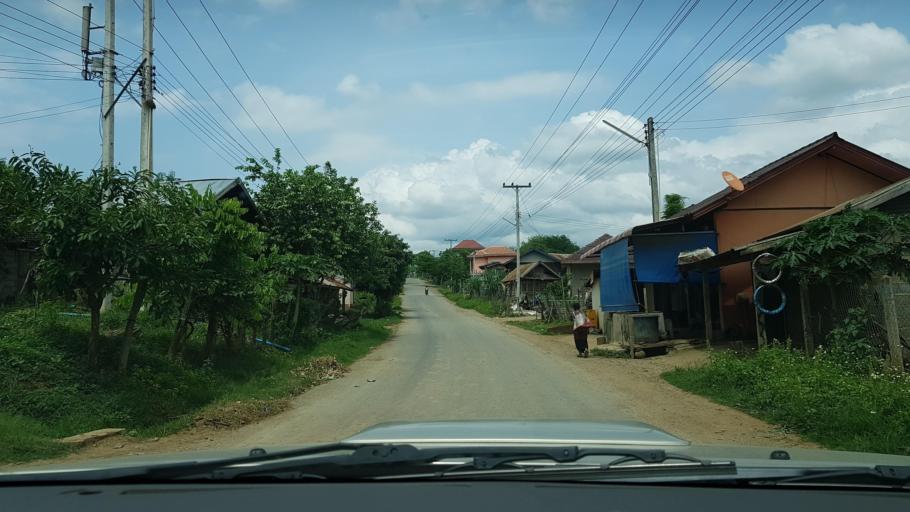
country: TH
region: Nan
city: Chaloem Phra Kiat
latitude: 20.0231
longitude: 101.3326
